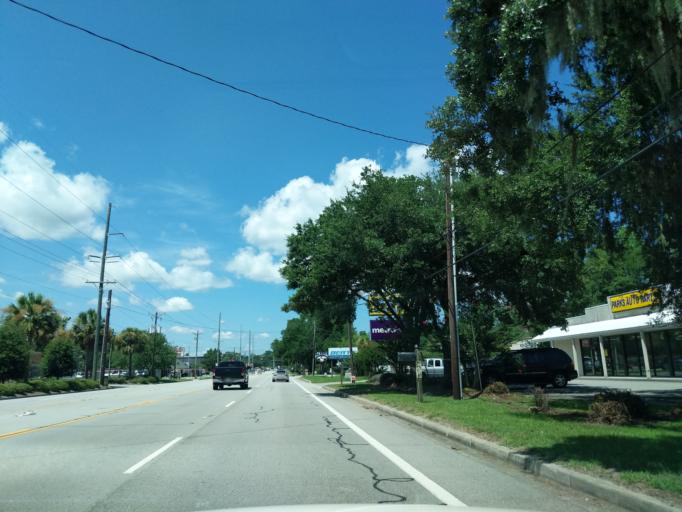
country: US
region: South Carolina
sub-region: Charleston County
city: Charleston
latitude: 32.7285
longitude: -79.9682
